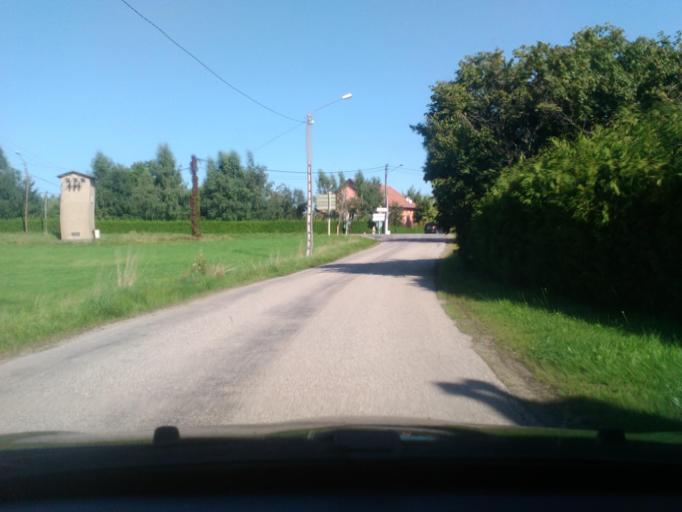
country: FR
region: Lorraine
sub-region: Departement des Vosges
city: Saint-Michel-sur-Meurthe
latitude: 48.3242
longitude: 6.8519
